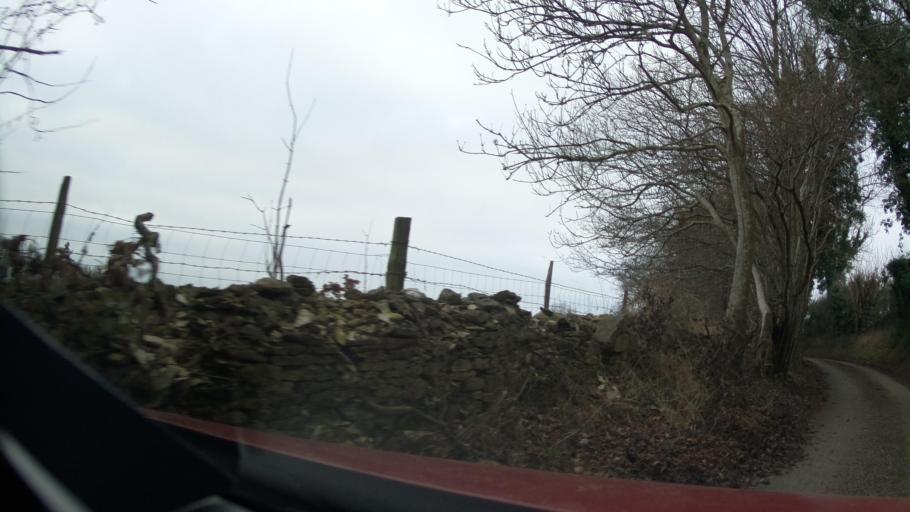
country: GB
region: England
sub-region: Wiltshire
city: Nettleton
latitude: 51.4889
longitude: -2.2428
